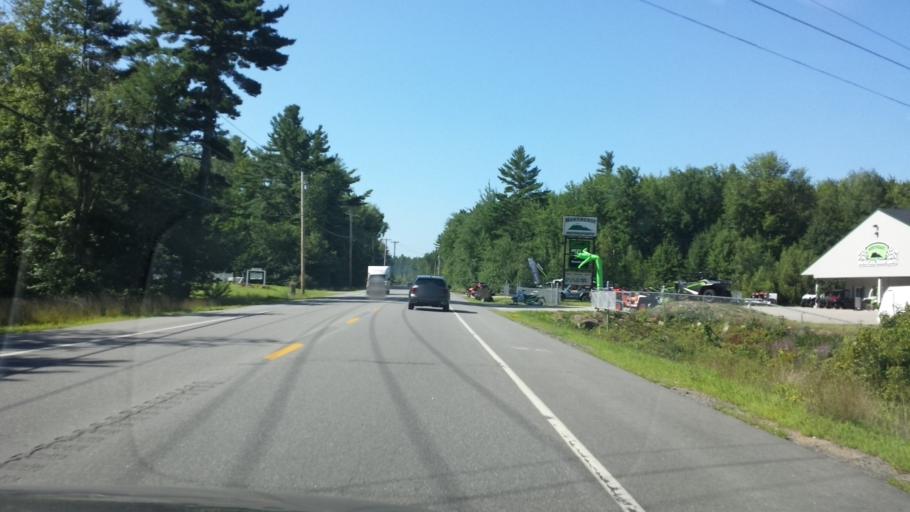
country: US
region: Maine
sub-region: York County
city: Lebanon
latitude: 43.4043
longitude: -70.8735
